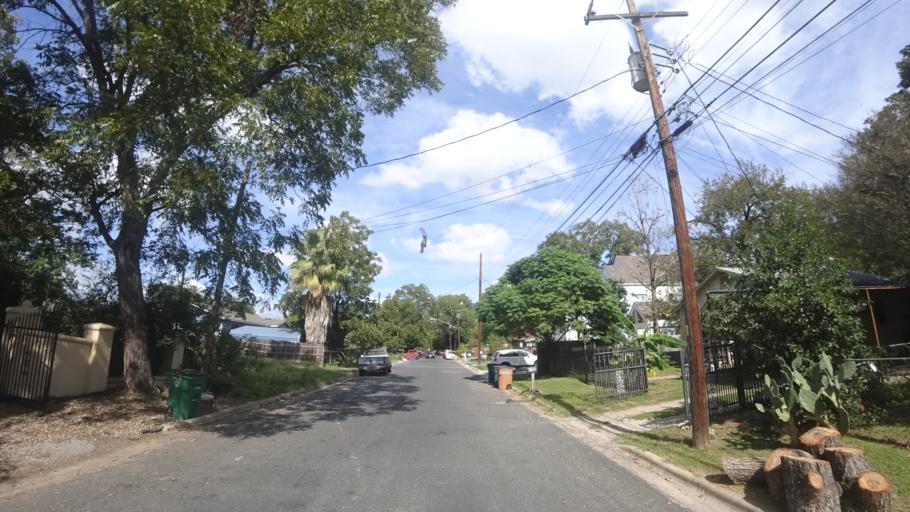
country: US
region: Texas
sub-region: Travis County
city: Austin
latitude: 30.2655
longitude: -97.7058
